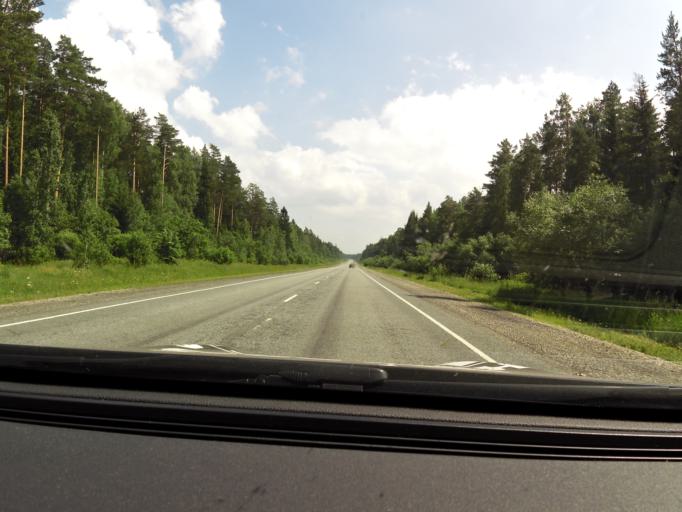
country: RU
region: Sverdlovsk
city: Achit
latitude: 56.8154
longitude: 57.8185
